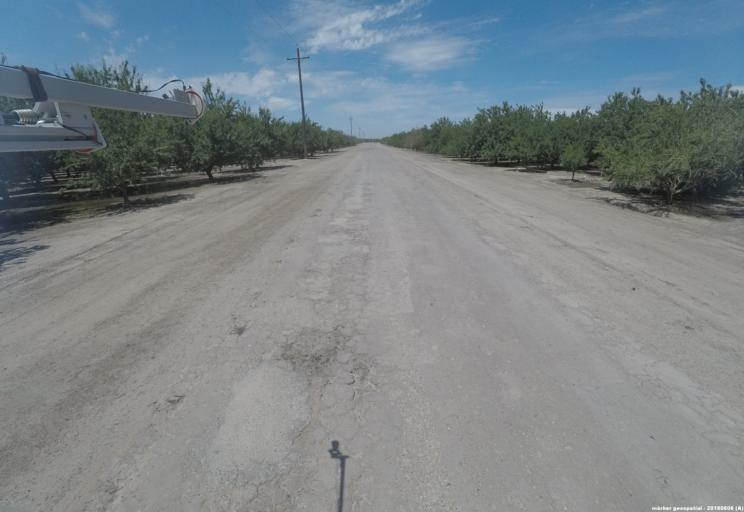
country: US
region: California
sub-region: Fresno County
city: Mendota
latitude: 36.8041
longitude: -120.3504
